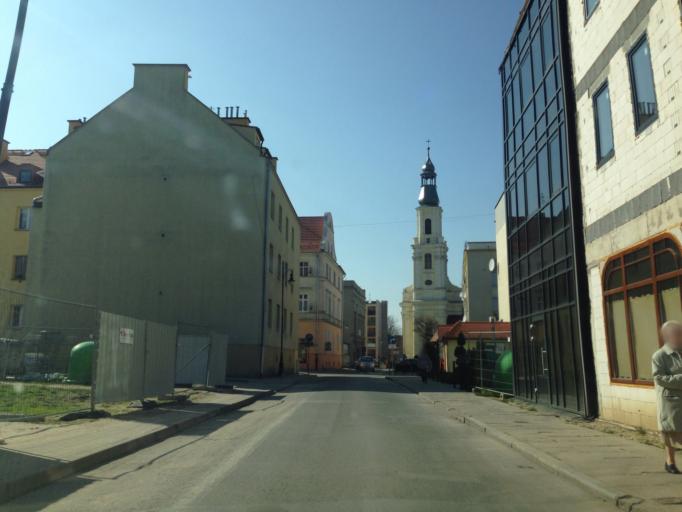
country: PL
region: Lower Silesian Voivodeship
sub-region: Powiat olesnicki
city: Olesnica
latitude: 51.2102
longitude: 17.3816
